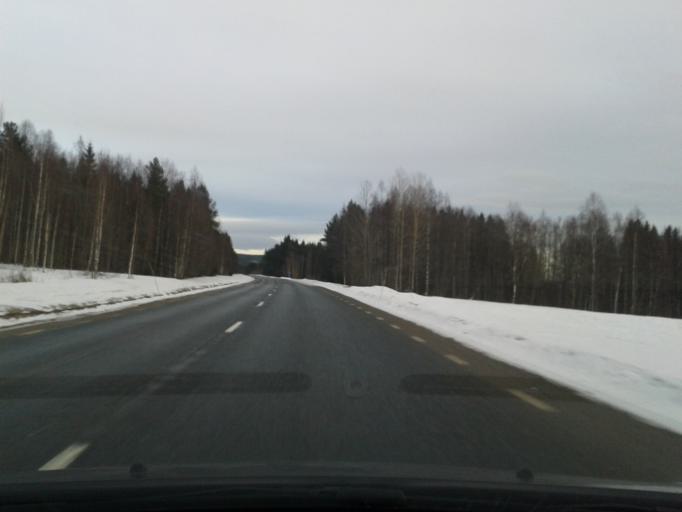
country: SE
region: Vaesternorrland
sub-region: Solleftea Kommun
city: As
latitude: 63.4432
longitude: 16.9159
